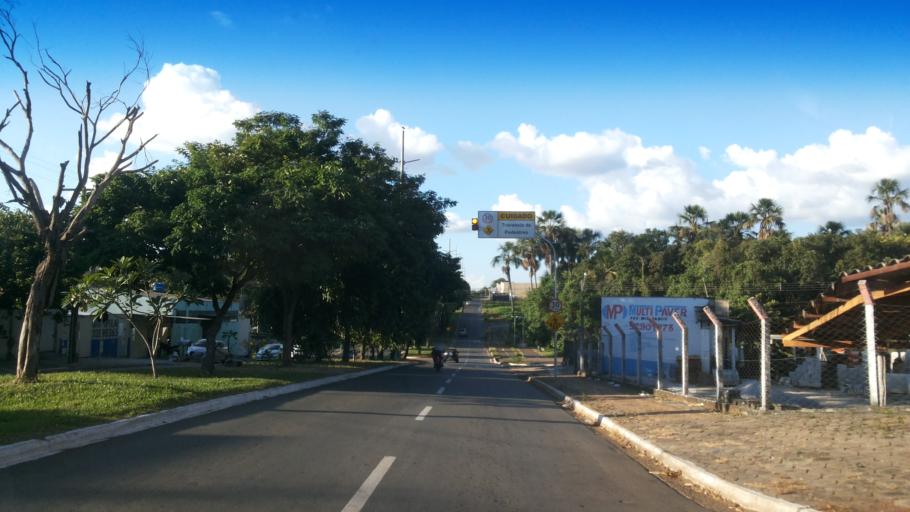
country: BR
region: Goias
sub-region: Goiania
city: Goiania
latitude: -16.7396
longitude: -49.3132
